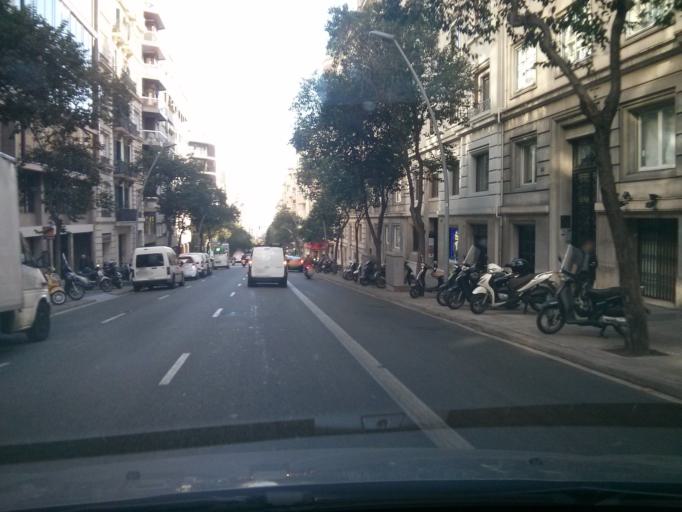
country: ES
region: Catalonia
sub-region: Provincia de Barcelona
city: Sarria-Sant Gervasi
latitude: 41.3995
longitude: 2.1423
